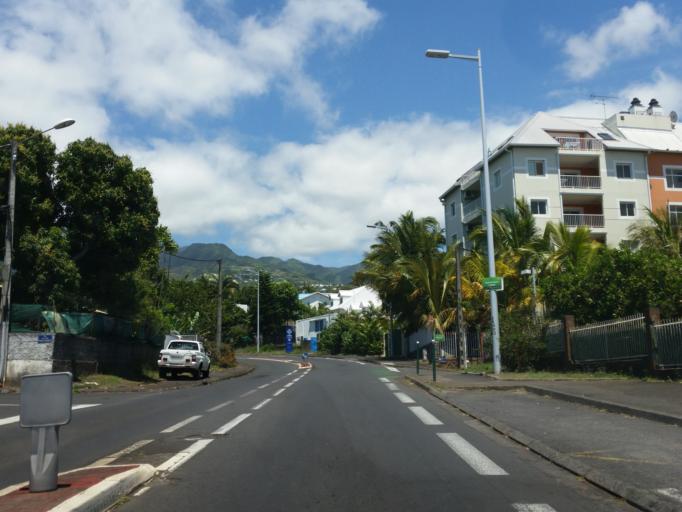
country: RE
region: Reunion
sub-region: Reunion
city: Saint-Denis
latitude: -20.9066
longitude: 55.4891
